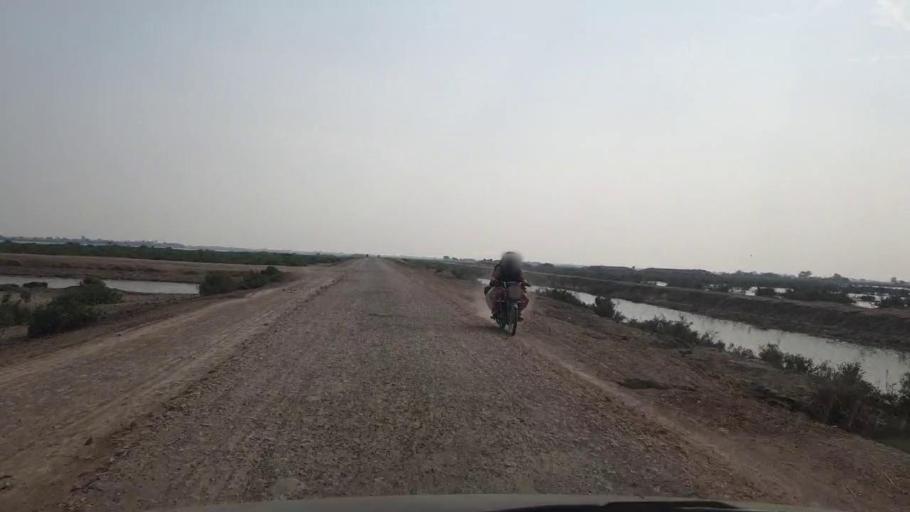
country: PK
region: Sindh
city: Tando Muhammad Khan
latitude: 25.0903
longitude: 68.3838
